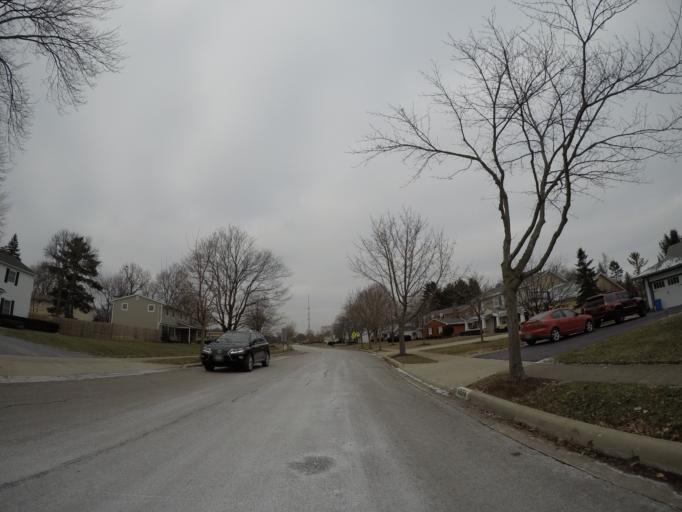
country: US
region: Ohio
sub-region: Franklin County
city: Upper Arlington
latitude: 40.0468
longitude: -83.0569
